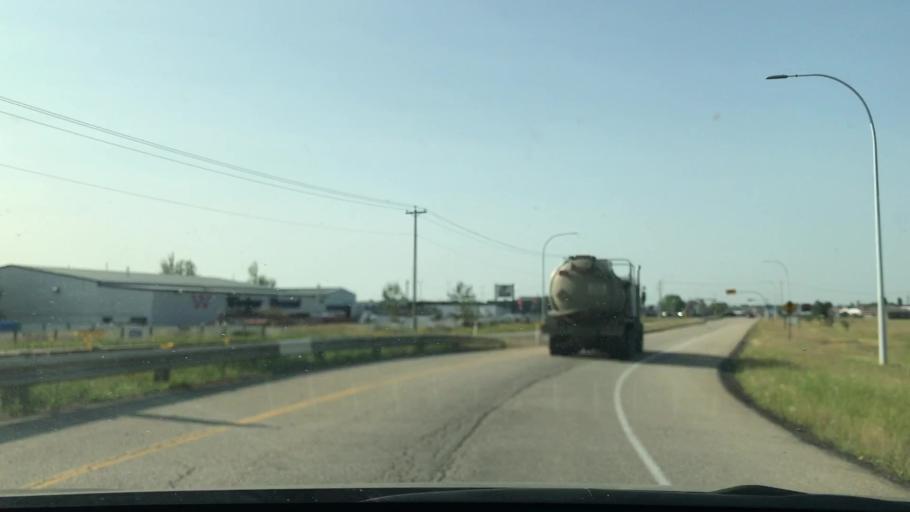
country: CA
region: Alberta
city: Leduc
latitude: 53.2827
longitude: -113.5475
